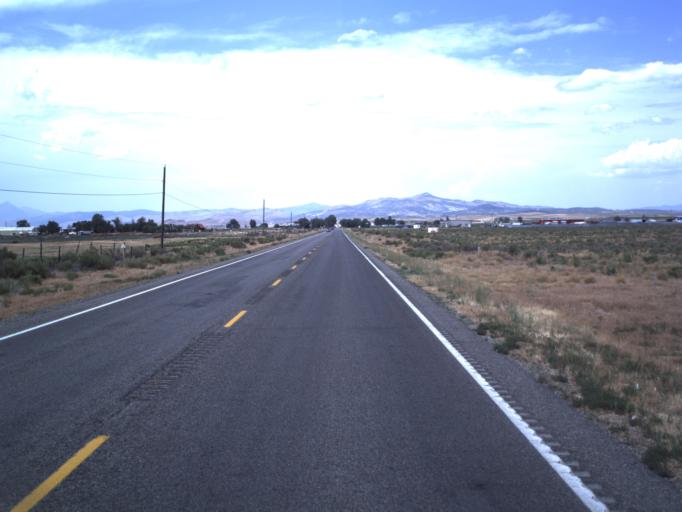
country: US
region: Utah
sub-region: Sanpete County
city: Moroni
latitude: 39.4551
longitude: -111.5626
